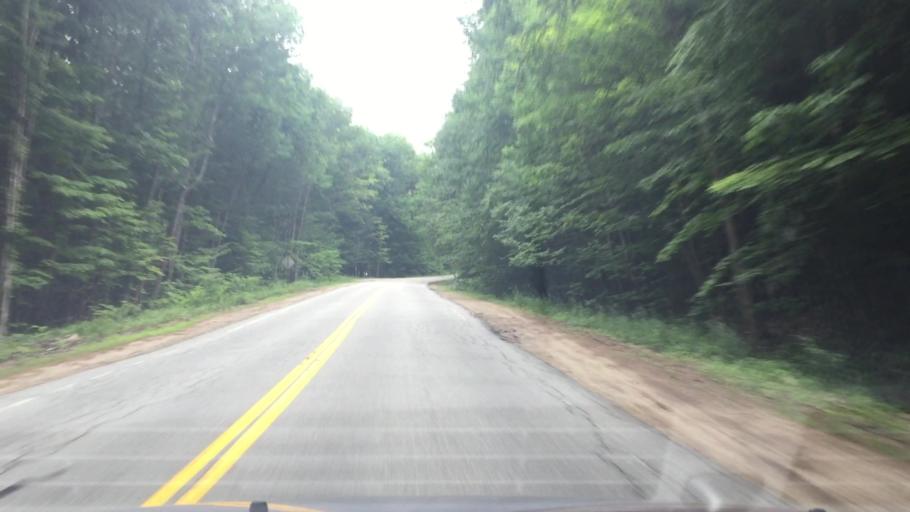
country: US
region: New Hampshire
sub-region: Carroll County
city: North Conway
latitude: 44.0983
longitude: -71.1731
